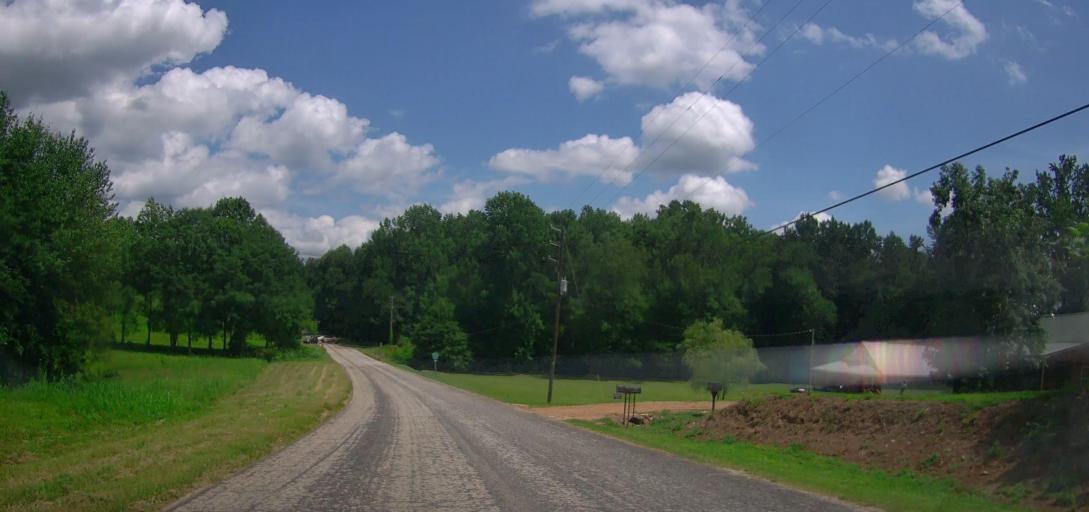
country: US
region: Georgia
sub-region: Carroll County
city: Bowdon
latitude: 33.5094
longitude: -85.3384
